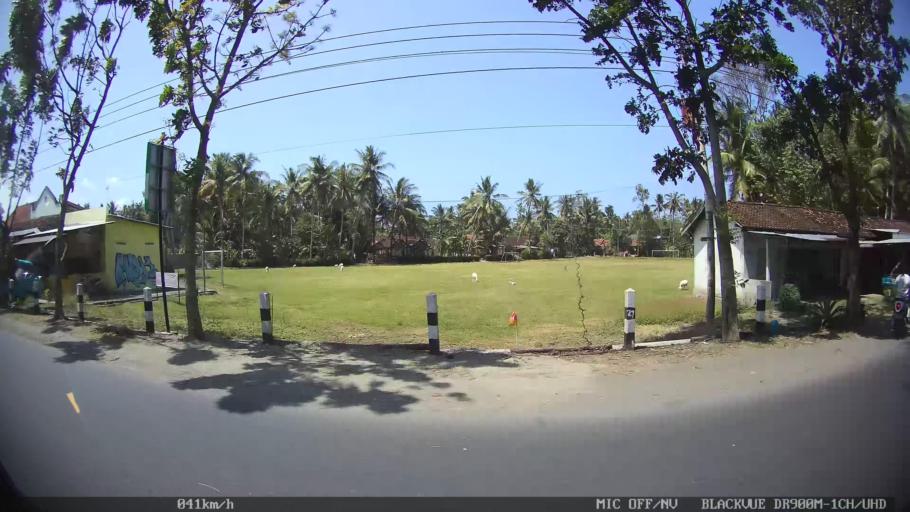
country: ID
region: Daerah Istimewa Yogyakarta
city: Srandakan
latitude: -7.9480
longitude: 110.2228
